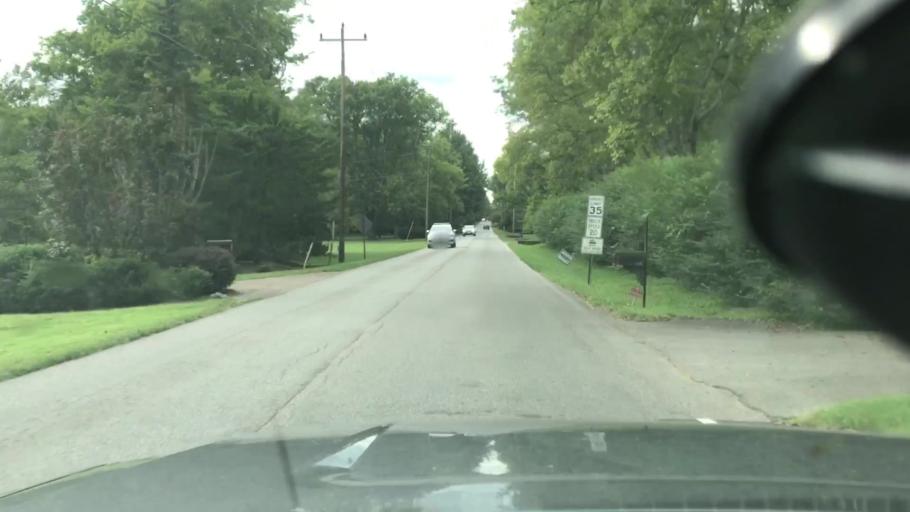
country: US
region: Tennessee
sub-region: Davidson County
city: Belle Meade
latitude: 36.0859
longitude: -86.8522
